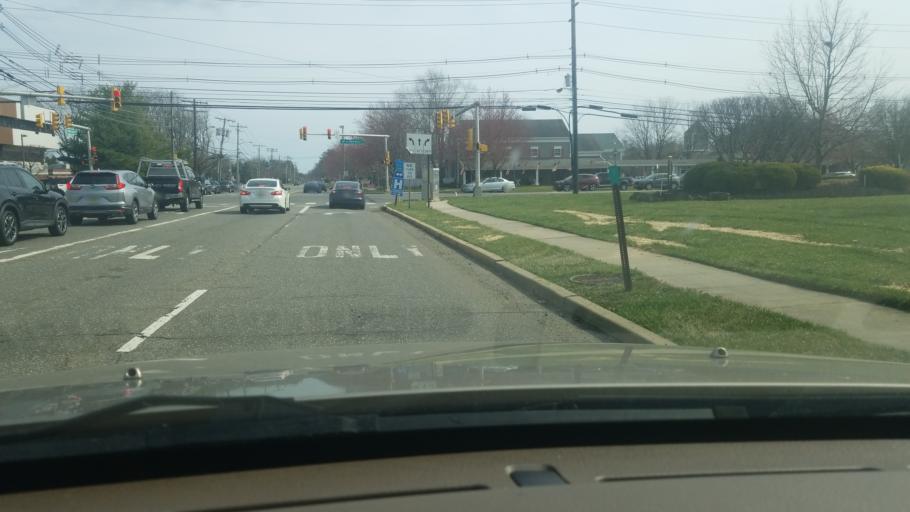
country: US
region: New Jersey
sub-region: Monmouth County
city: West Freehold
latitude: 40.2423
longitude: -74.3027
